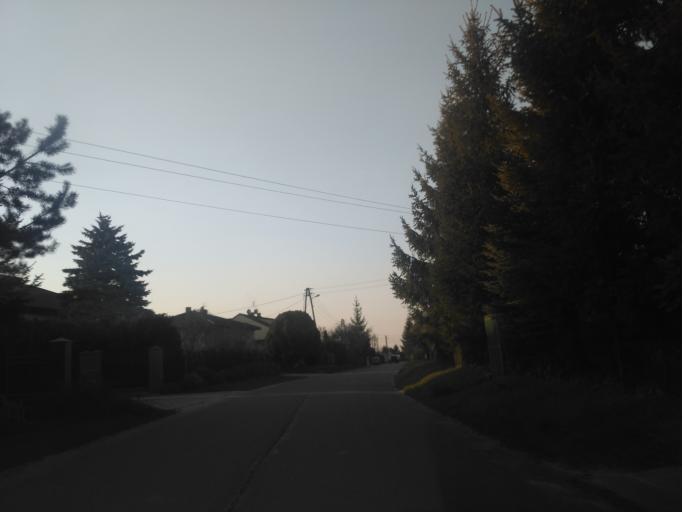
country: PL
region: Lublin Voivodeship
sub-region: Powiat chelmski
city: Pokrowka
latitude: 51.1111
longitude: 23.4835
